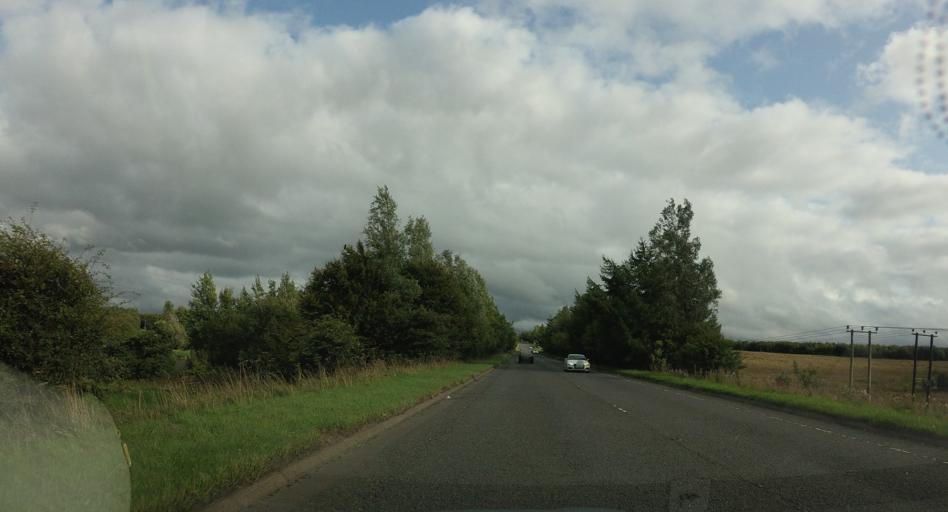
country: GB
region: Scotland
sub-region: West Lothian
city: Whitburn
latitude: 55.8837
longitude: -3.6671
